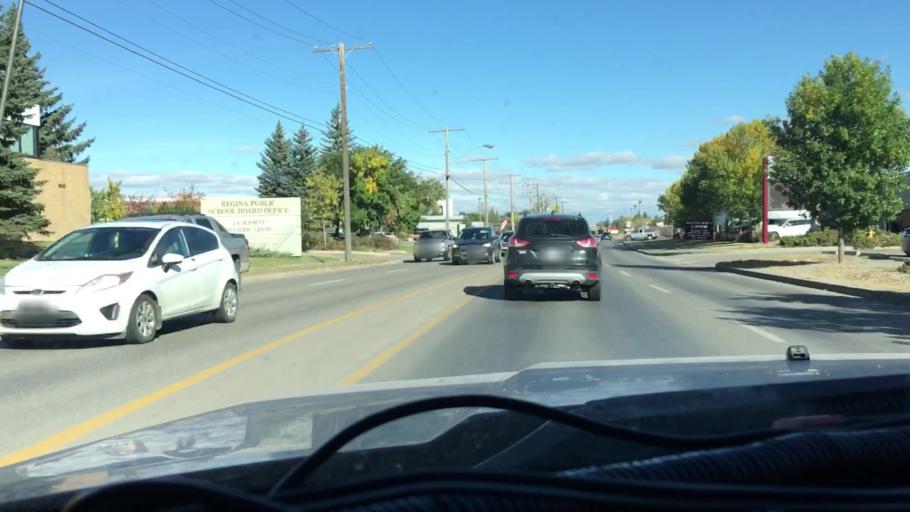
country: CA
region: Saskatchewan
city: Regina
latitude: 50.4629
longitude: -104.6041
